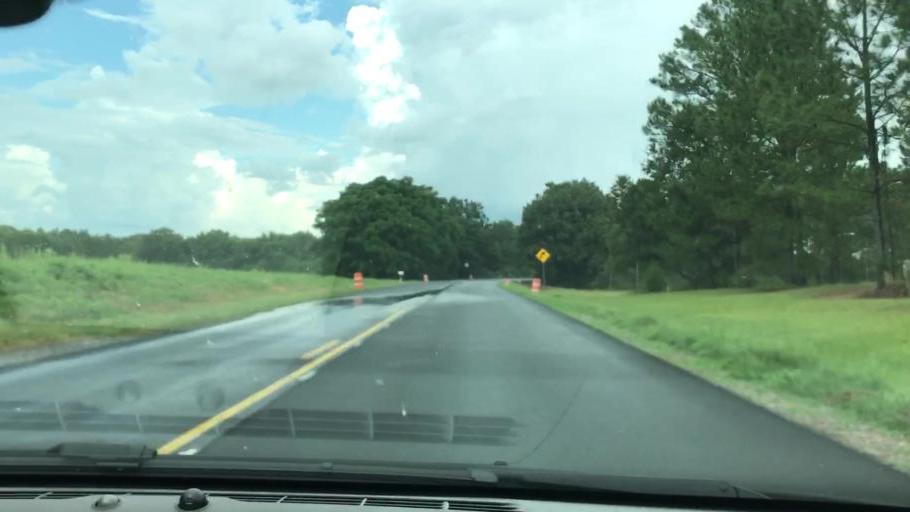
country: US
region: Georgia
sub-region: Early County
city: Blakely
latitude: 31.4055
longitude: -84.9611
